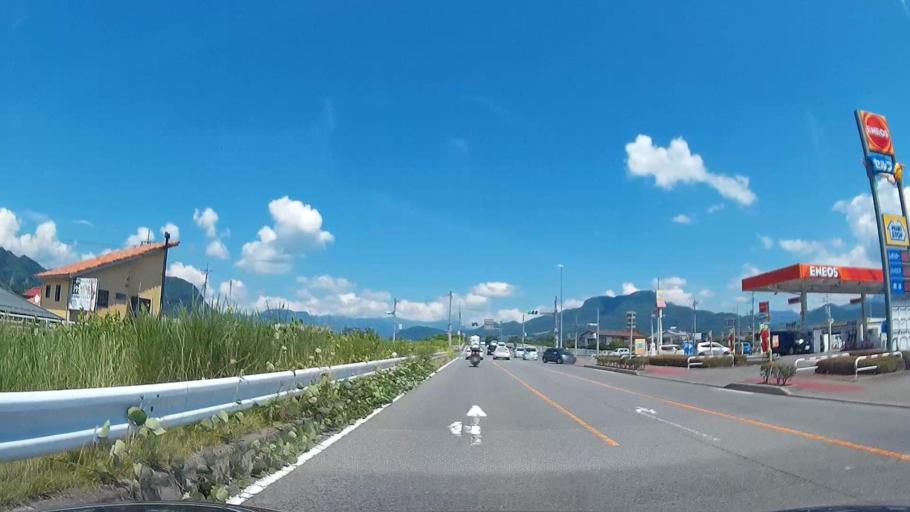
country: JP
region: Gunma
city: Numata
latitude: 36.6439
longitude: 139.0290
